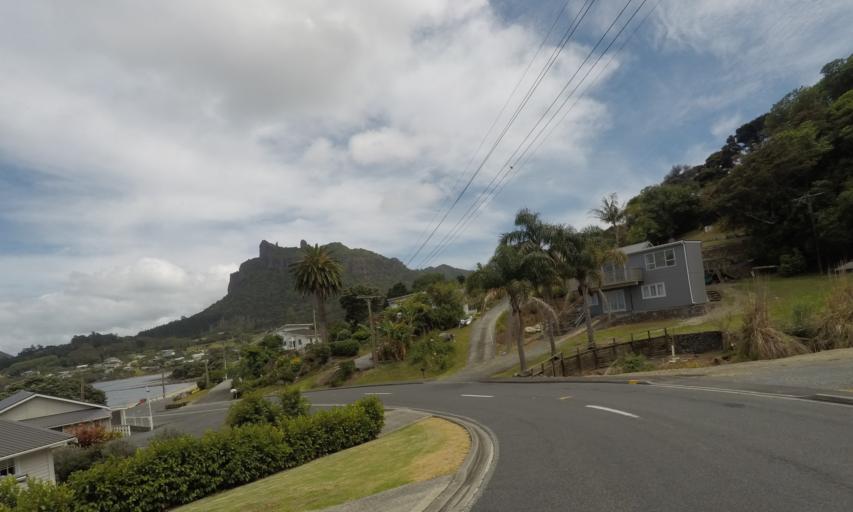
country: NZ
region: Northland
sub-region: Whangarei
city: Ruakaka
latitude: -35.8285
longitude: 174.5303
